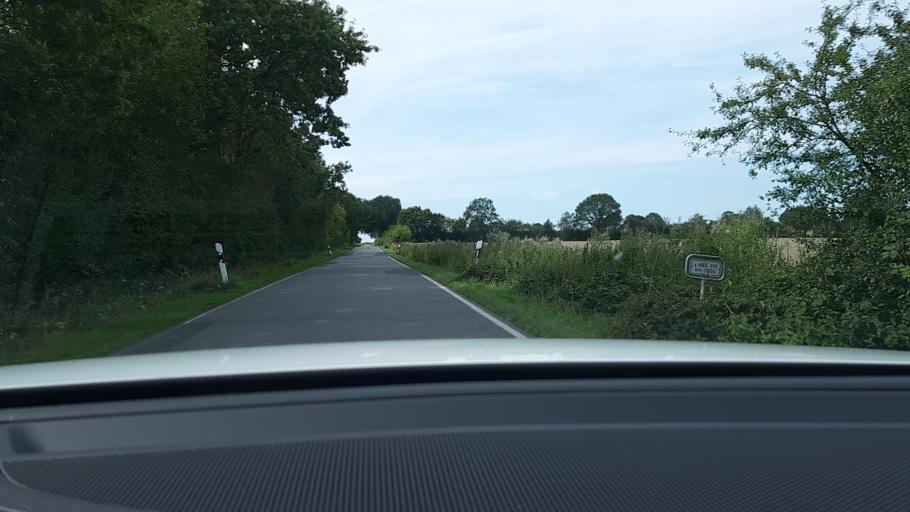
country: DE
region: Schleswig-Holstein
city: Heidekamp
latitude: 53.8683
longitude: 10.4932
